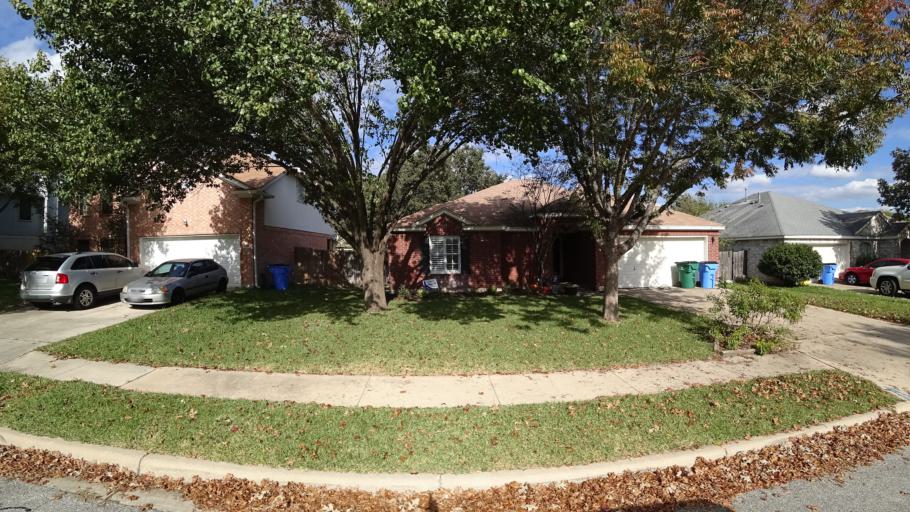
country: US
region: Texas
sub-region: Travis County
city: Pflugerville
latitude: 30.4351
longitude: -97.6345
